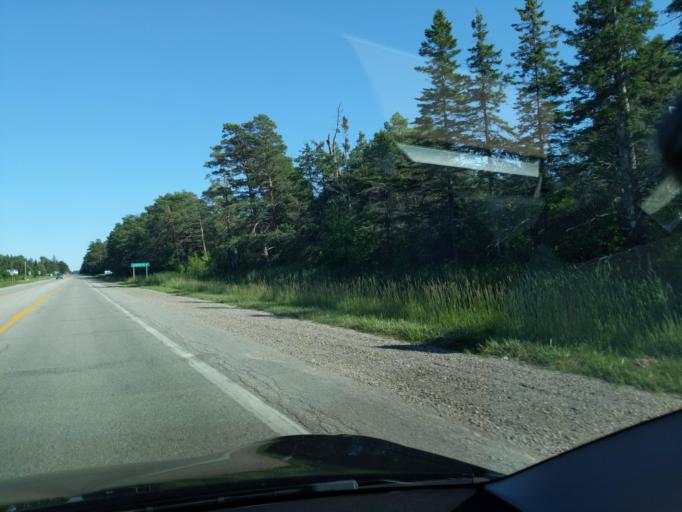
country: US
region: Michigan
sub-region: Mackinac County
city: Saint Ignace
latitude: 45.7624
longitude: -84.7139
